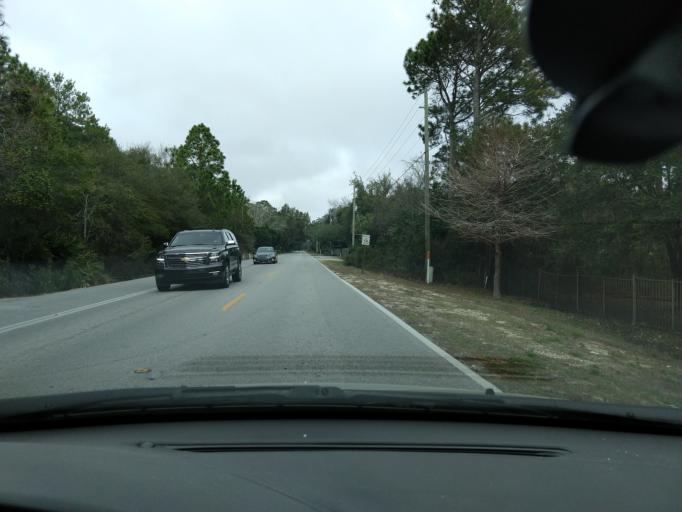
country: US
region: Florida
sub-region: Walton County
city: Miramar Beach
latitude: 30.3934
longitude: -86.3044
